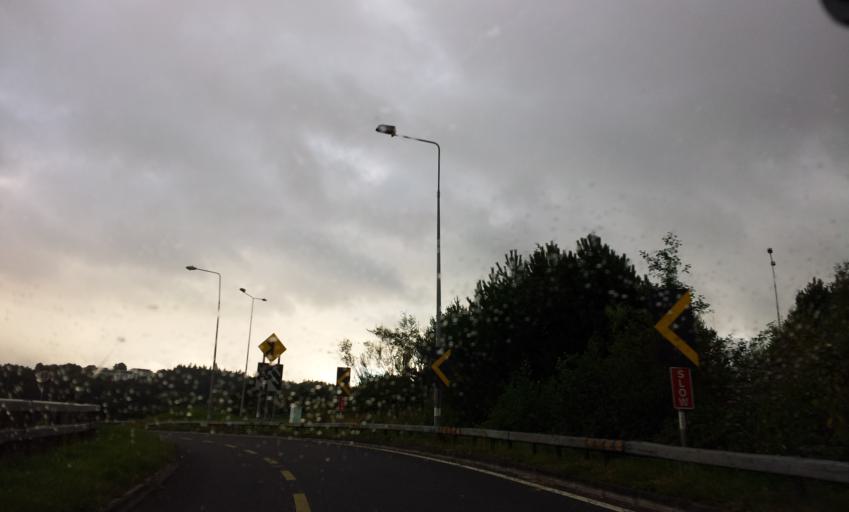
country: IE
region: Munster
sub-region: County Cork
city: Cork
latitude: 51.8799
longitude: -8.4174
